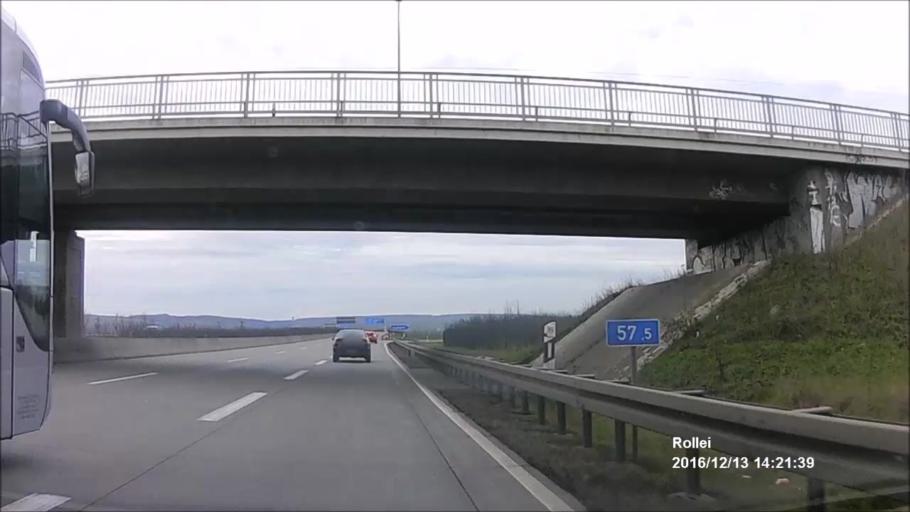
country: DE
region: Thuringia
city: Noda
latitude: 51.0327
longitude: 11.0017
